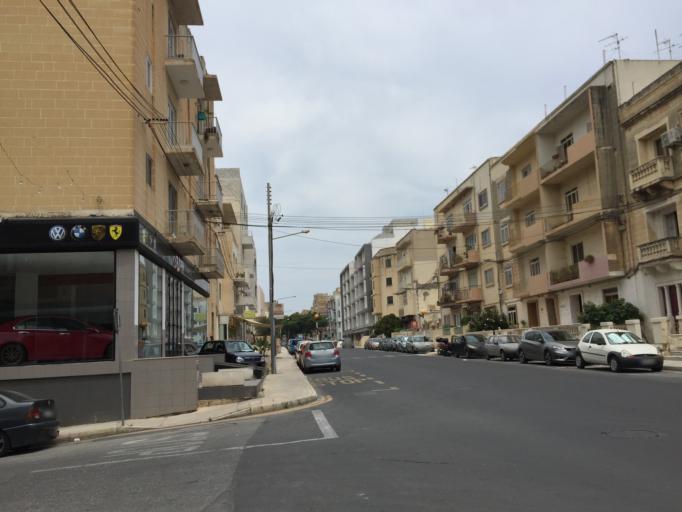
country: MT
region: Tal-Pieta
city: Pieta
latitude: 35.8910
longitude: 14.4921
